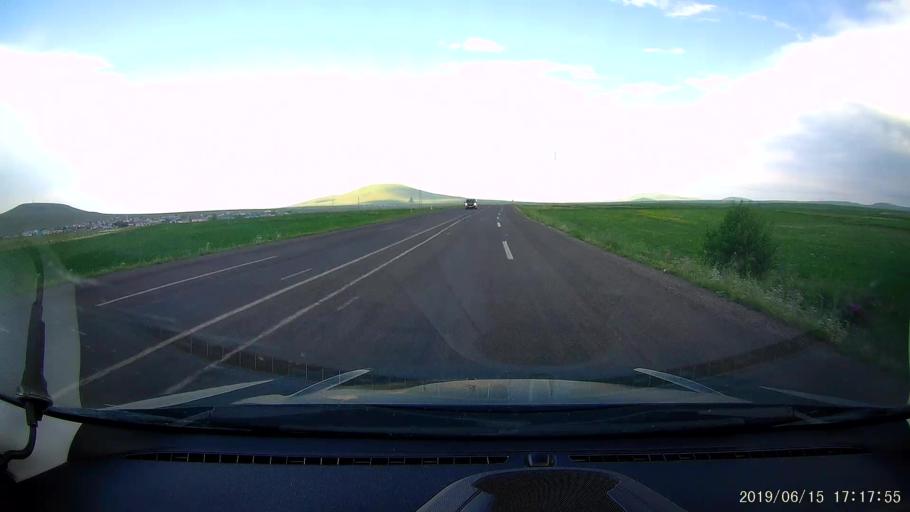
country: TR
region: Kars
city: Kars
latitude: 40.6145
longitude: 43.2476
